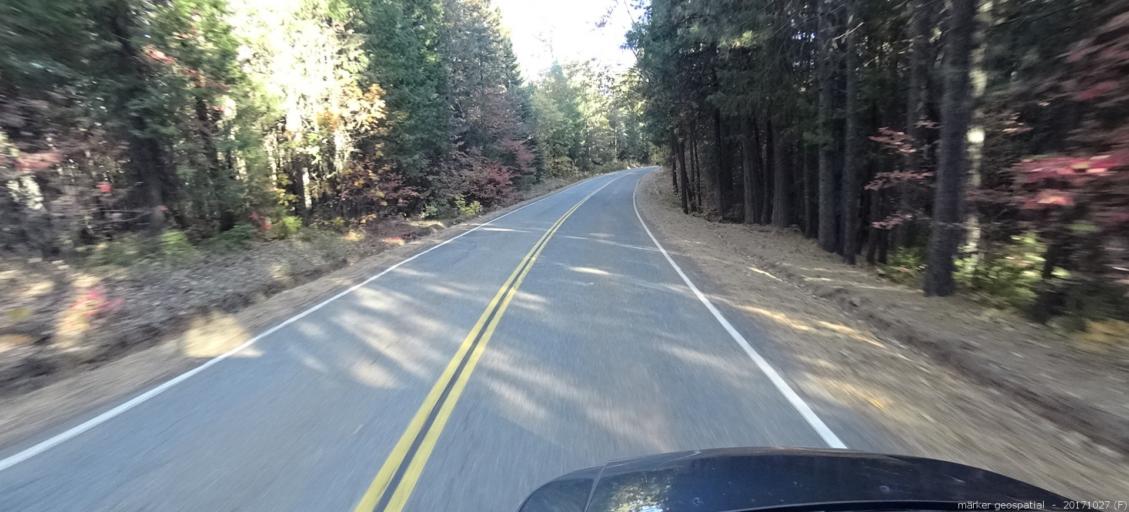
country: US
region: California
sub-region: Shasta County
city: Burney
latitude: 40.9726
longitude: -121.9302
